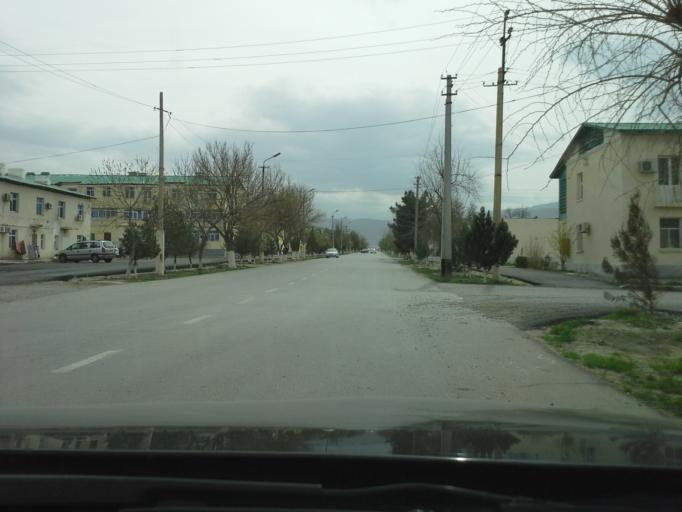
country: TM
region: Ahal
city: Abadan
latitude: 38.0589
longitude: 58.1571
